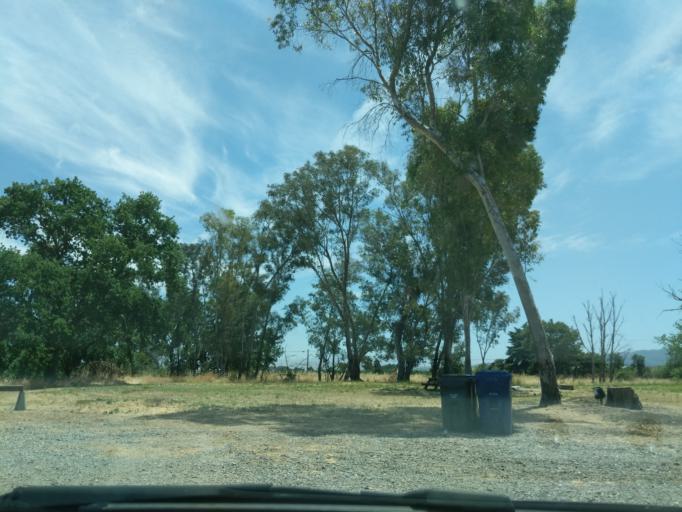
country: US
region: California
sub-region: Santa Clara County
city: Gilroy
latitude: 37.0492
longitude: -121.5627
